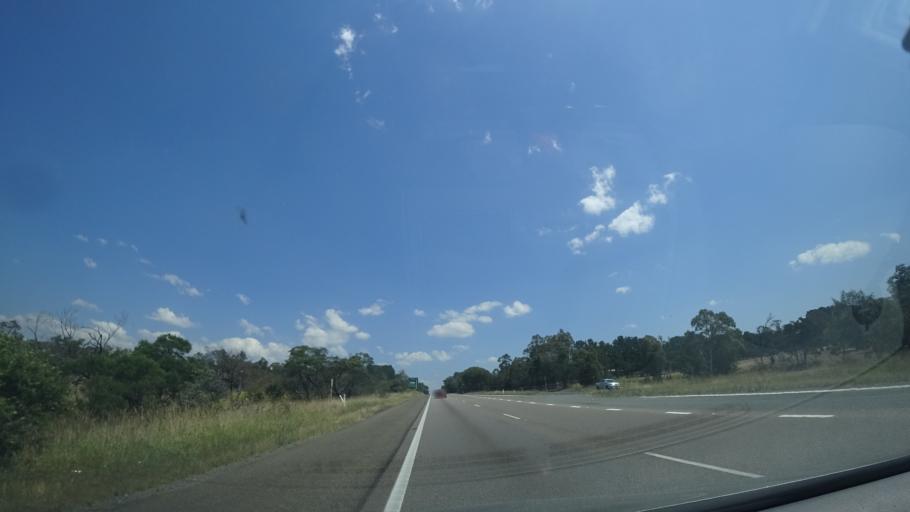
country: AU
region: New South Wales
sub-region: Wingecarribee
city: Bundanoon
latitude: -34.5969
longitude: 150.2400
